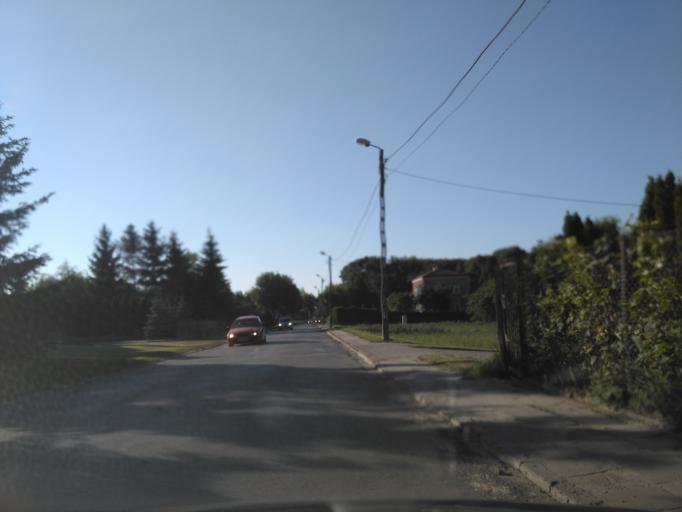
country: PL
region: Lublin Voivodeship
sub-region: Powiat lubelski
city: Bychawa
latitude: 51.0204
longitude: 22.5219
